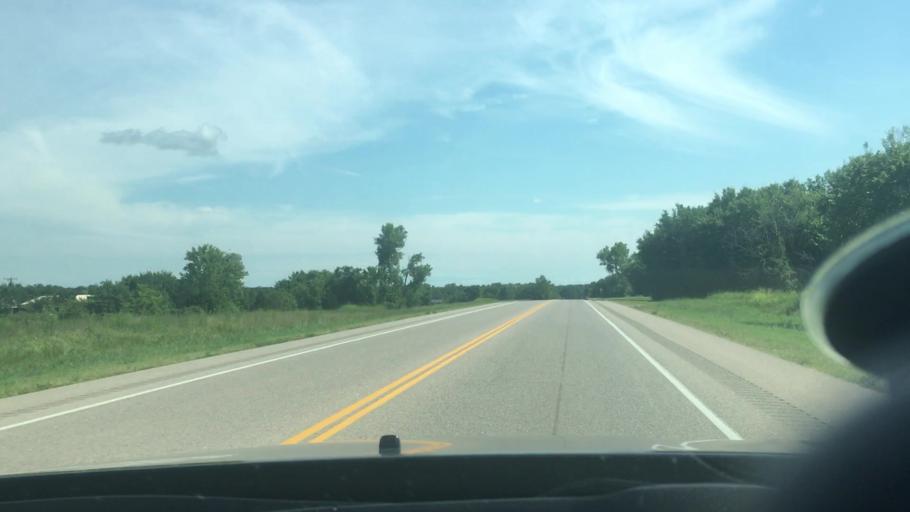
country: US
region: Oklahoma
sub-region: Seminole County
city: Seminole
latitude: 35.1565
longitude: -96.6747
